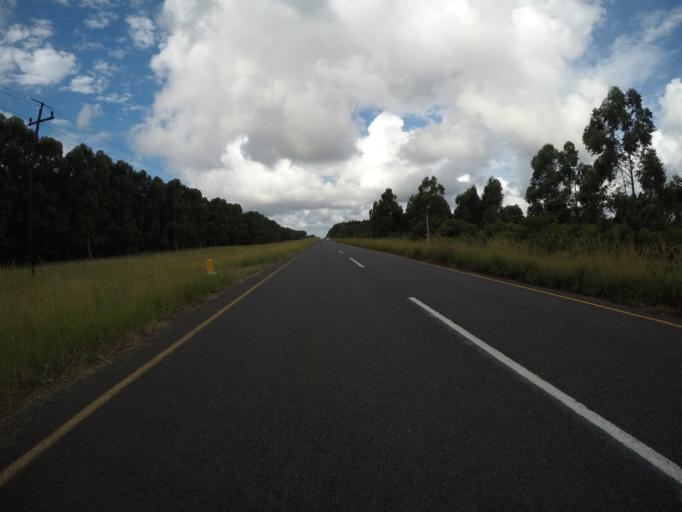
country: ZA
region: KwaZulu-Natal
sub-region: uMkhanyakude District Municipality
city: Mtubatuba
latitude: -28.3949
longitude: 32.2196
